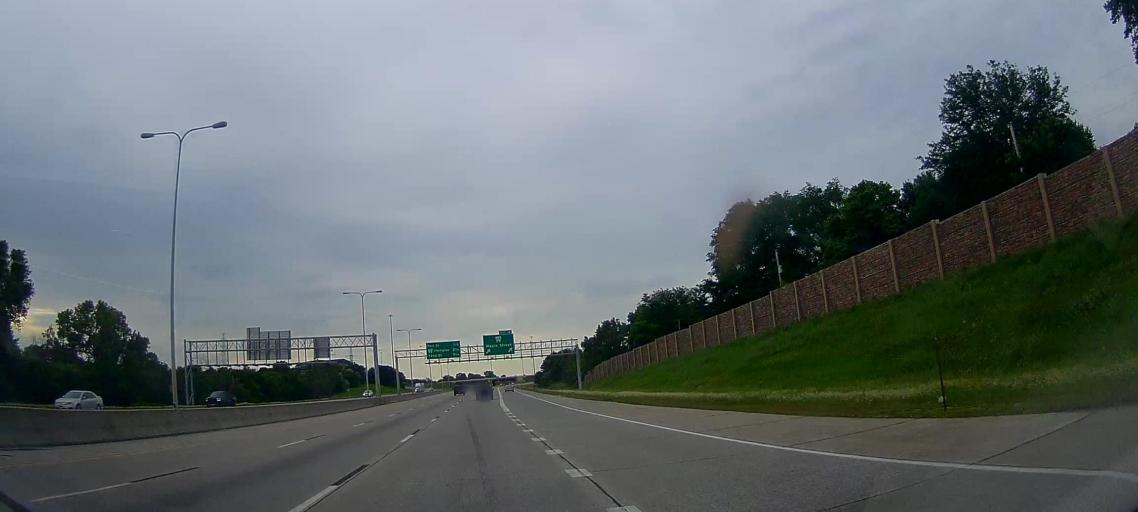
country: US
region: Nebraska
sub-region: Douglas County
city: Ralston
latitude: 41.2796
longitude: -96.0758
